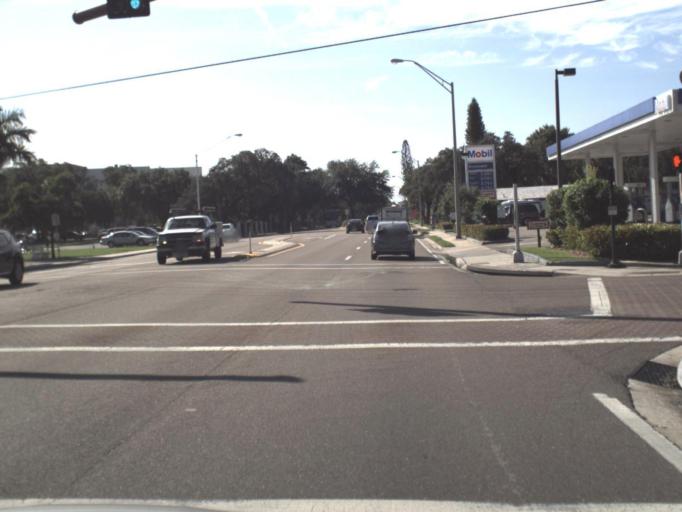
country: US
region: Florida
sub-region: Sarasota County
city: Sarasota
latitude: 27.3601
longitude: -82.5493
